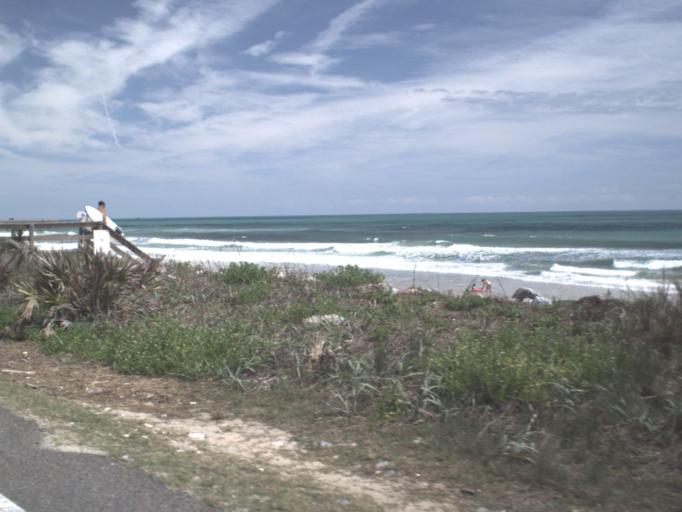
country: US
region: Florida
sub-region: Flagler County
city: Flagler Beach
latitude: 29.4750
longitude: -81.1245
